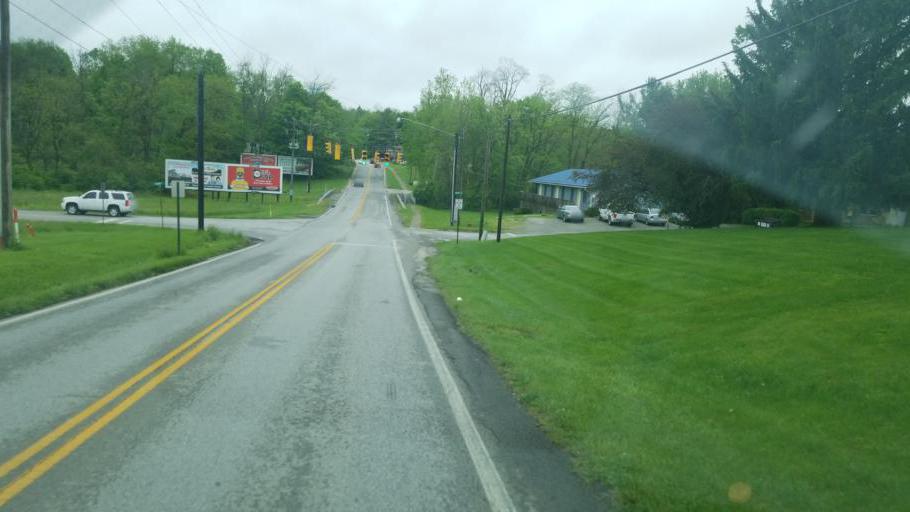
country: US
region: Ohio
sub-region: Highland County
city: Hillsboro
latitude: 39.2169
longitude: -83.6163
